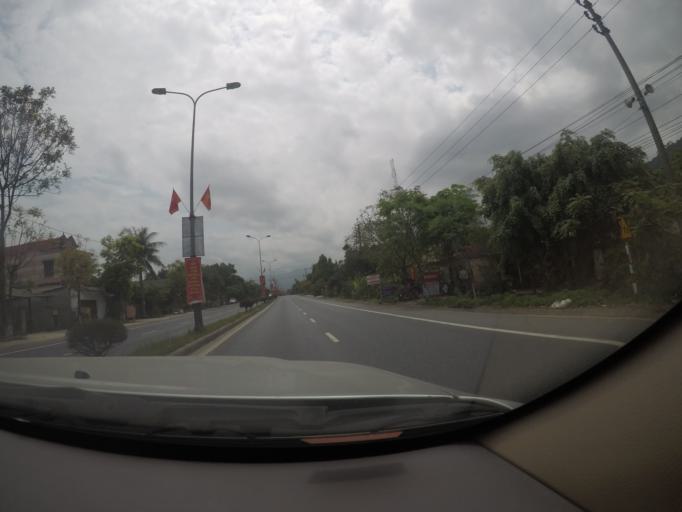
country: VN
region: Thua Thien-Hue
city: Phu Loc
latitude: 16.2837
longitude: 107.8578
